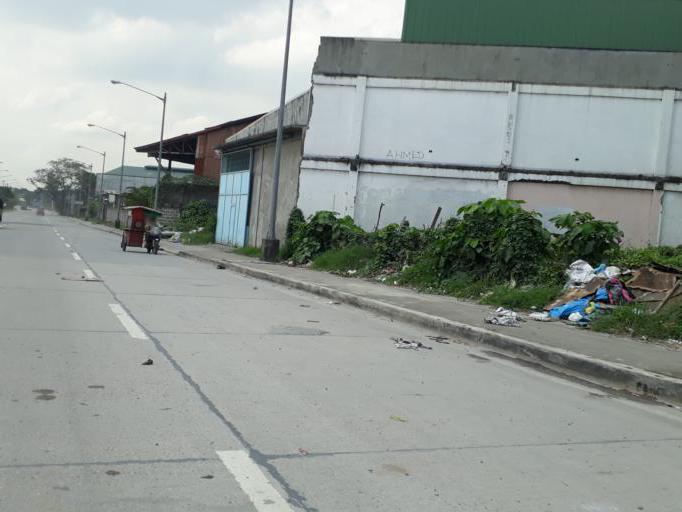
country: PH
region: Calabarzon
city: Bagong Pagasa
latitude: 14.7033
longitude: 121.0145
